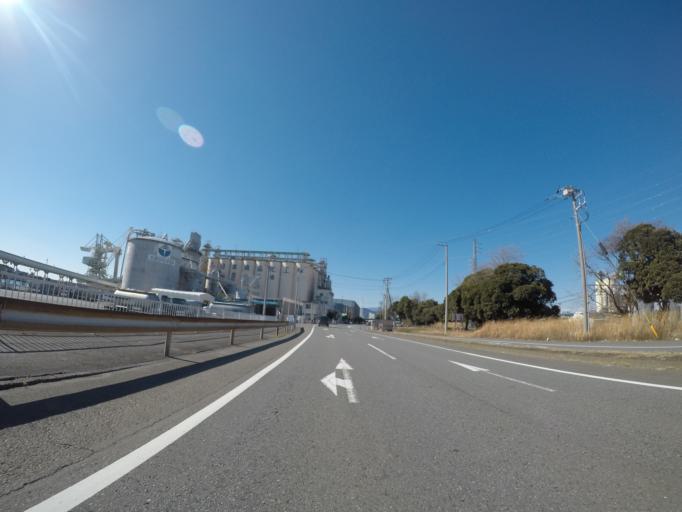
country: JP
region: Shizuoka
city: Fuji
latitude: 35.1450
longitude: 138.6943
